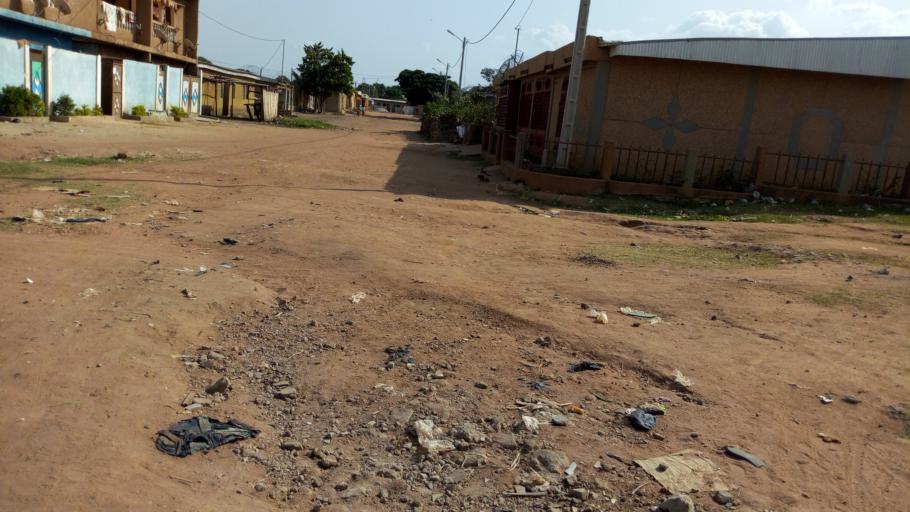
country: CI
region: Vallee du Bandama
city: Bouake
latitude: 7.7080
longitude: -5.0433
